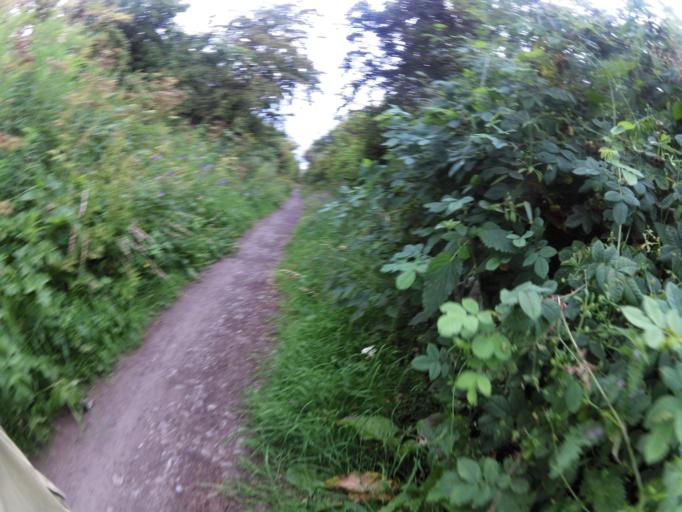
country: GB
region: Scotland
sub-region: Edinburgh
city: Kirkliston
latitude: 55.9511
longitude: -3.4008
